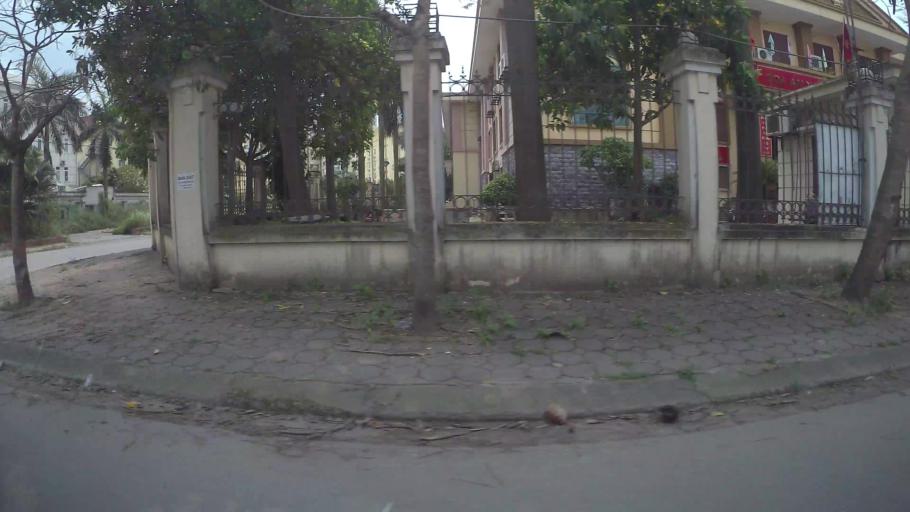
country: VN
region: Ha Noi
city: Trau Quy
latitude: 21.0693
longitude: 105.9104
